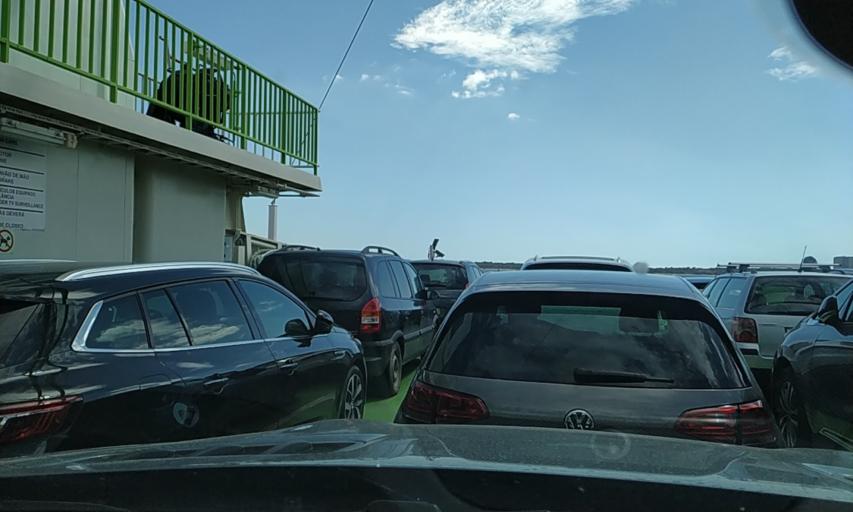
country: PT
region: Setubal
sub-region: Setubal
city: Setubal
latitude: 38.5041
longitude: -8.8855
